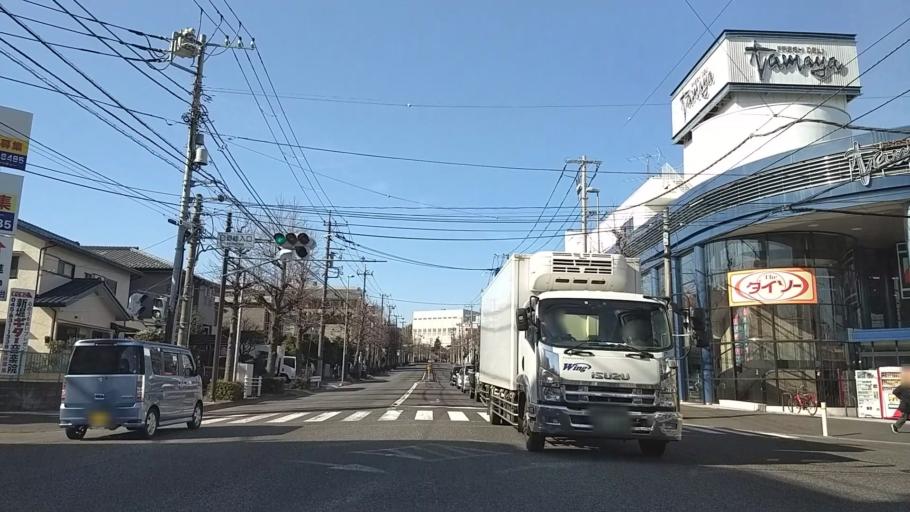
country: JP
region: Kanagawa
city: Kamakura
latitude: 35.3681
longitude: 139.5905
